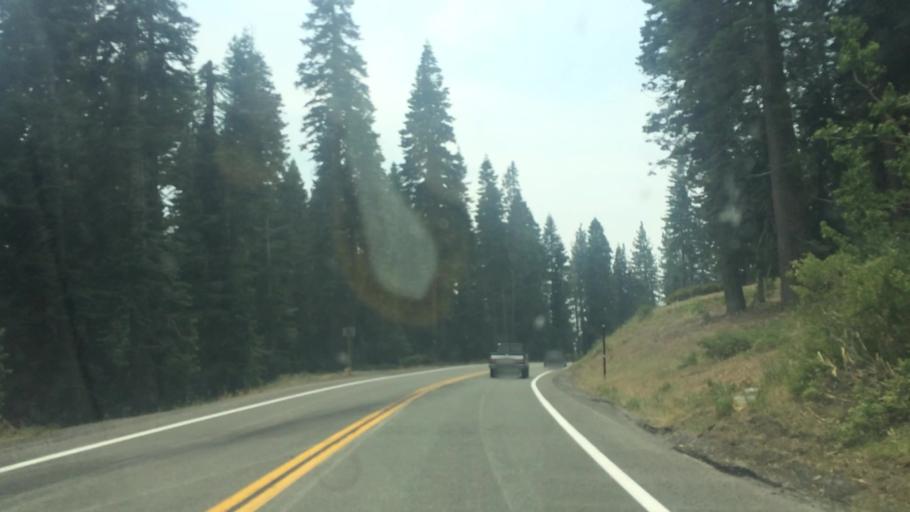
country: US
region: California
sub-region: Calaveras County
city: Arnold
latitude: 38.5984
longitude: -120.2229
